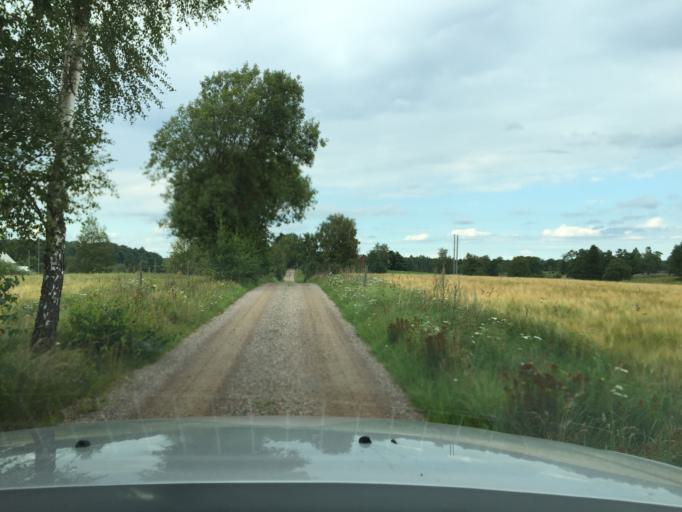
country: SE
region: Skane
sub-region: Hassleholms Kommun
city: Sosdala
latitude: 56.0495
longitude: 13.6897
